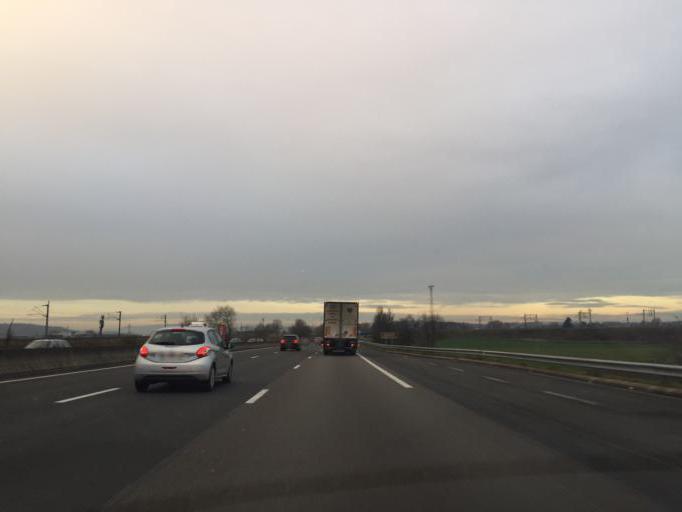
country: FR
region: Bourgogne
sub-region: Departement de Saone-et-Loire
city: Creches-sur-Saone
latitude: 46.2695
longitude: 4.7888
